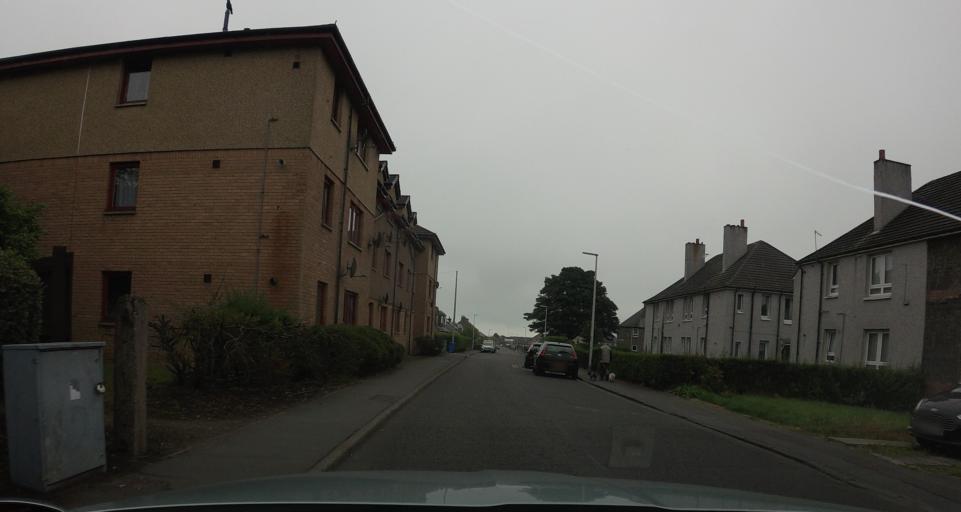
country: GB
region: Scotland
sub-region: Fife
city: Kelty
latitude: 56.1350
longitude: -3.3885
